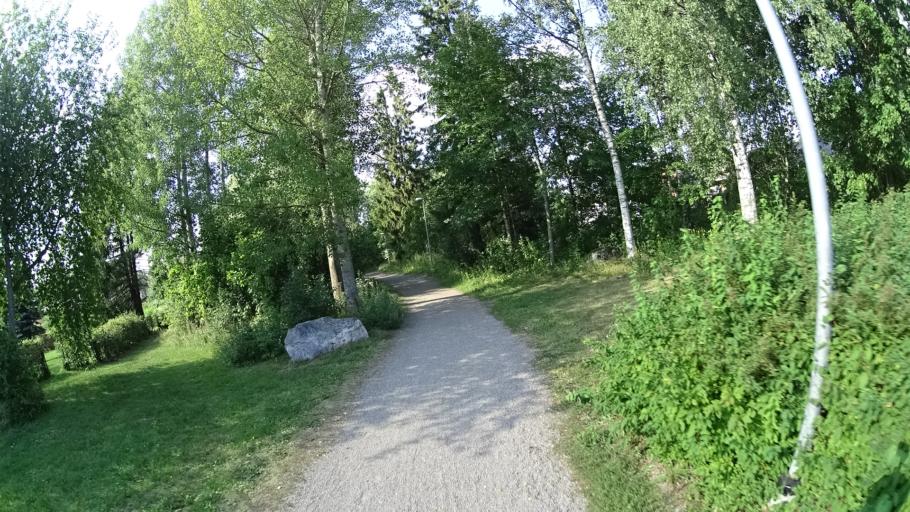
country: FI
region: Uusimaa
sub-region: Porvoo
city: Porvoo
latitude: 60.4096
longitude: 25.6624
